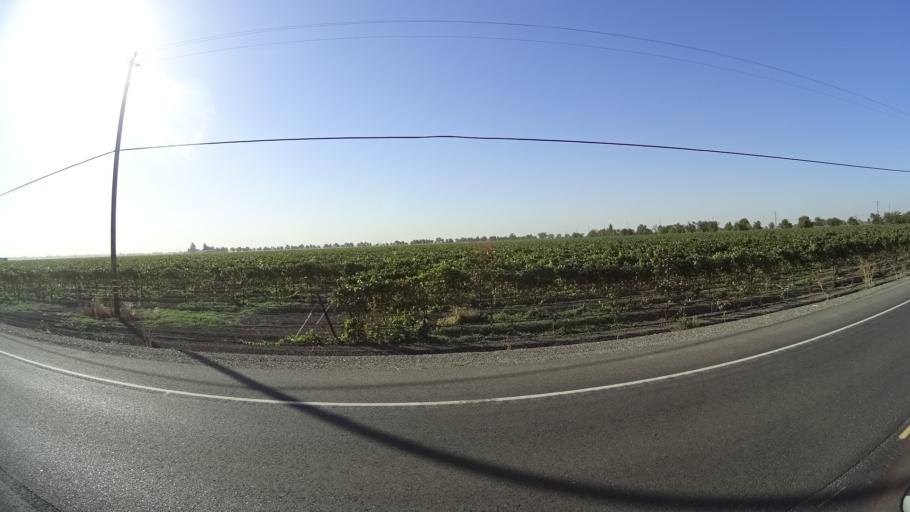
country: US
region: California
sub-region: Sacramento County
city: Parkway
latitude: 38.4144
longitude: -121.5806
